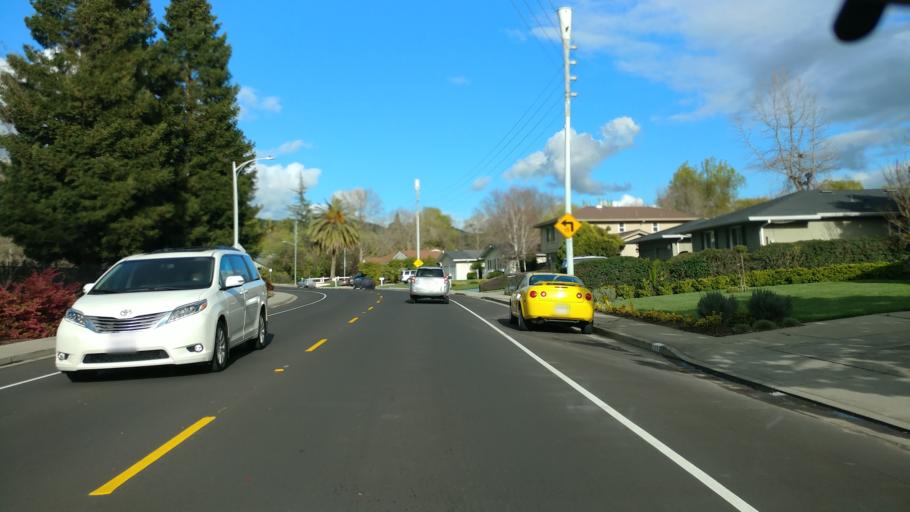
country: US
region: California
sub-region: Contra Costa County
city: San Ramon
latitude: 37.7957
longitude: -121.9754
